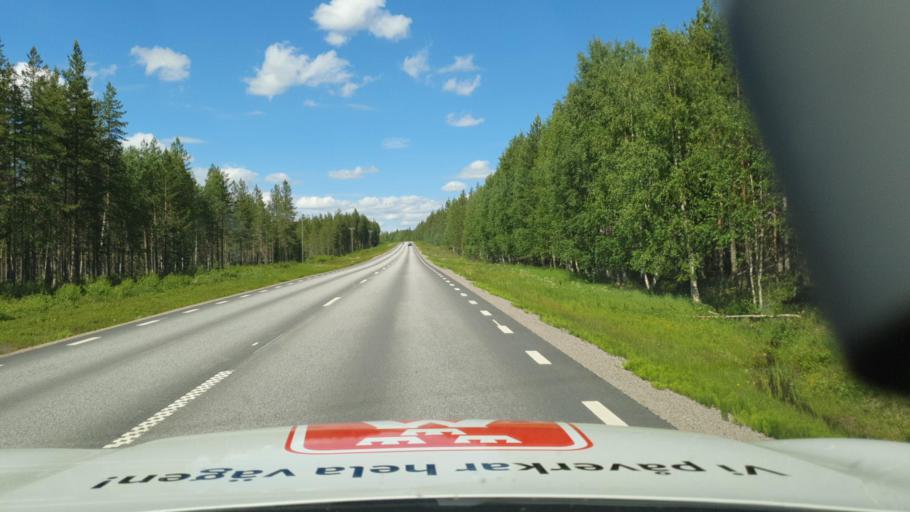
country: SE
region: Vaesterbotten
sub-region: Skelleftea Kommun
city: Langsele
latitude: 64.9493
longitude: 20.2686
